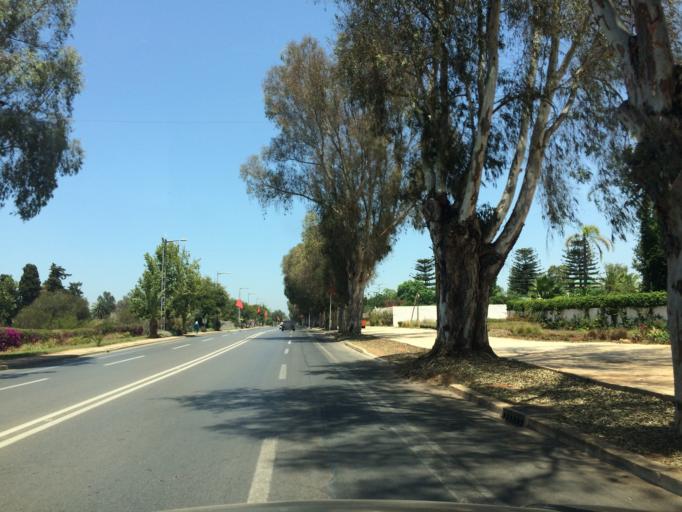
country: MA
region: Rabat-Sale-Zemmour-Zaer
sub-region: Rabat
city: Rabat
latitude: 33.9417
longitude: -6.8214
